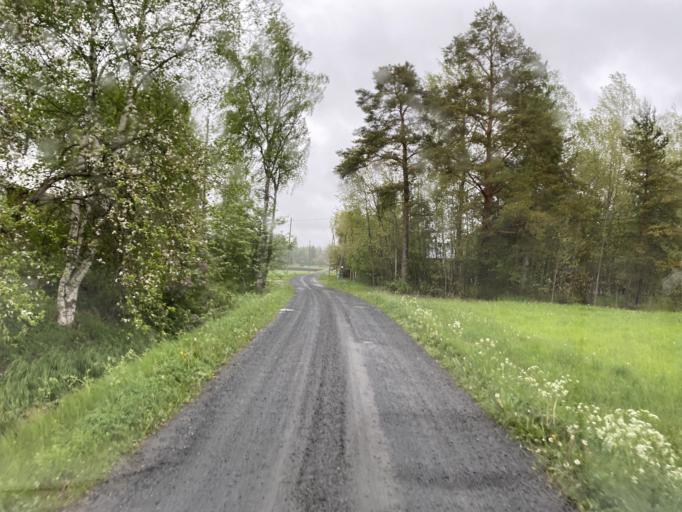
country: FI
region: Pirkanmaa
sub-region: Etelae-Pirkanmaa
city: Urjala
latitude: 60.9488
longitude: 23.5469
